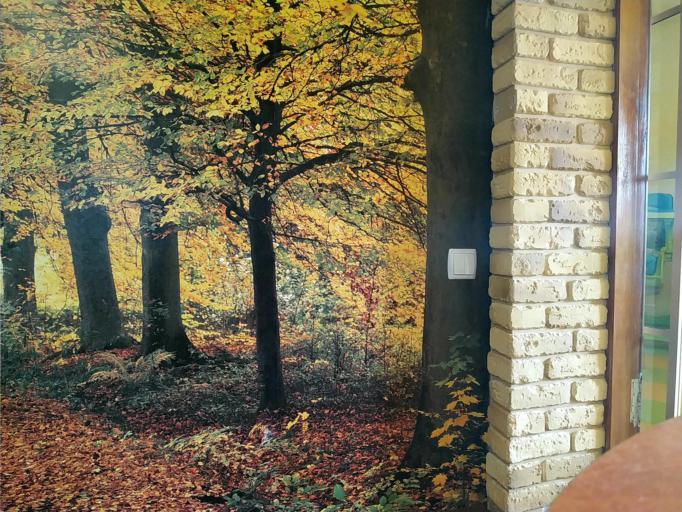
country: RU
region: Smolensk
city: Katyn'
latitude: 54.8862
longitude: 31.7998
